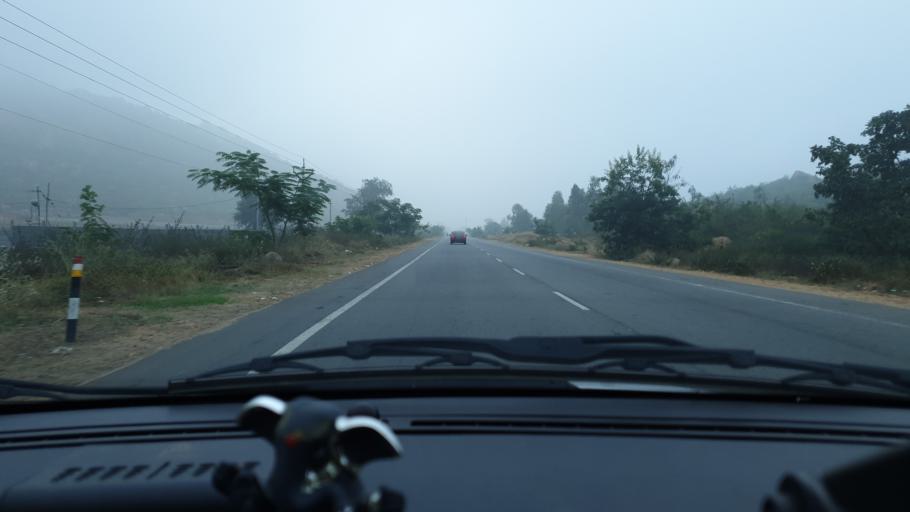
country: IN
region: Telangana
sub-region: Mahbubnagar
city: Farrukhnagar
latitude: 16.9119
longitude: 78.5274
